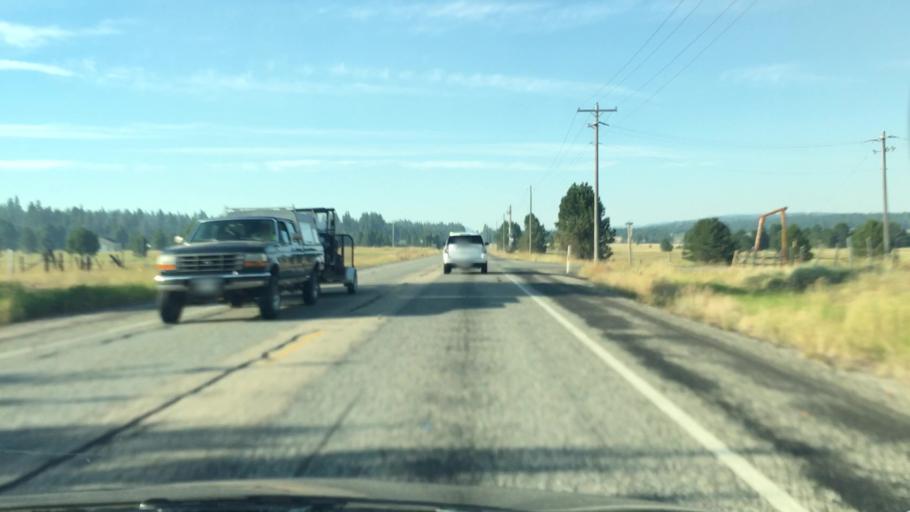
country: US
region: Idaho
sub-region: Valley County
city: Cascade
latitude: 44.3514
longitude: -116.0248
